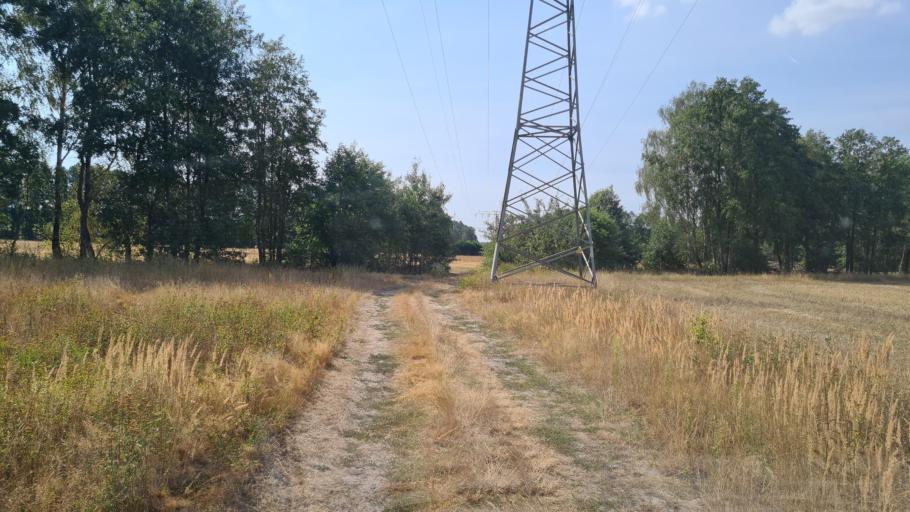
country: DE
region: Brandenburg
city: Finsterwalde
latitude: 51.6592
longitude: 13.7520
